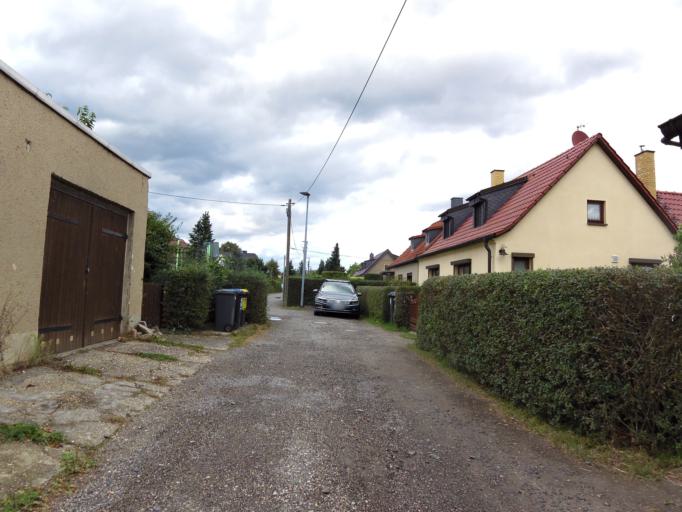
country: DE
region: Saxony
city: Schkeuditz
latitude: 51.3484
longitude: 12.2876
